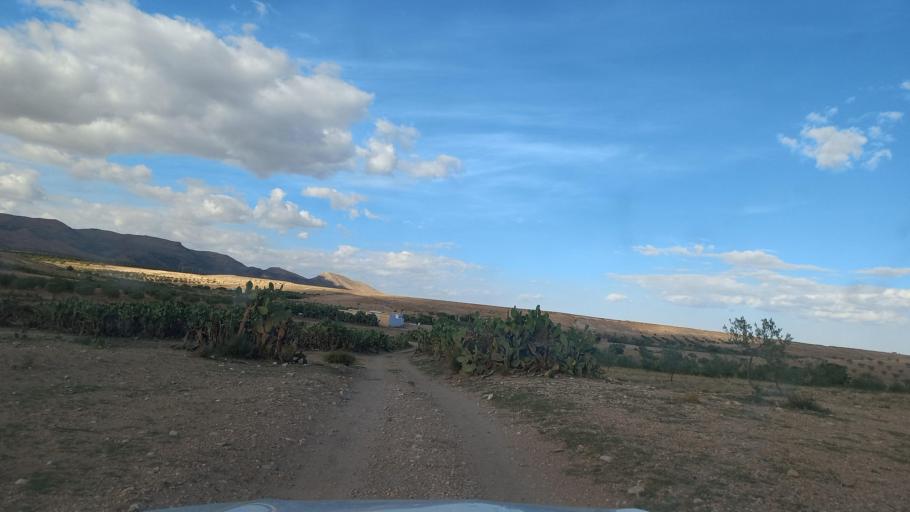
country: TN
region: Al Qasrayn
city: Sbiba
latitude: 35.3975
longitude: 9.0160
